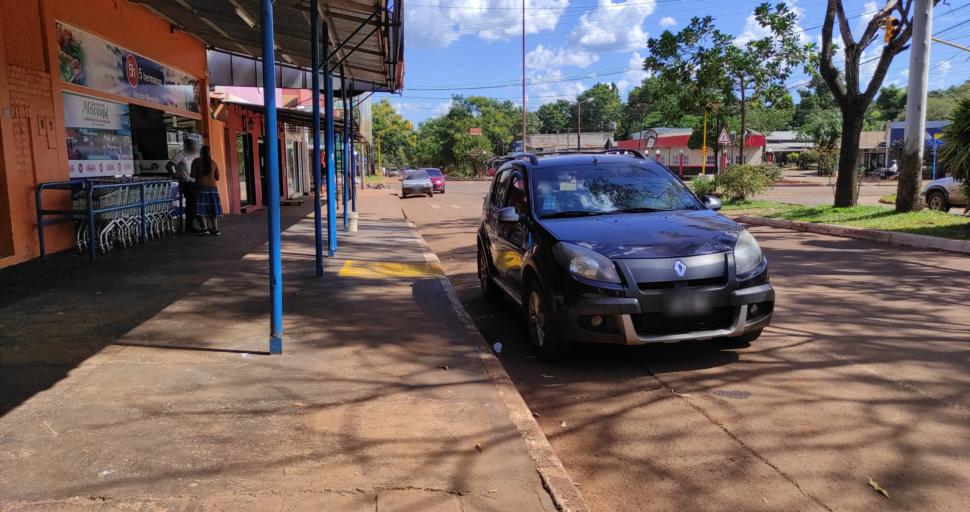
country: AR
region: Misiones
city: El Soberbio
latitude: -27.2961
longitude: -54.1980
